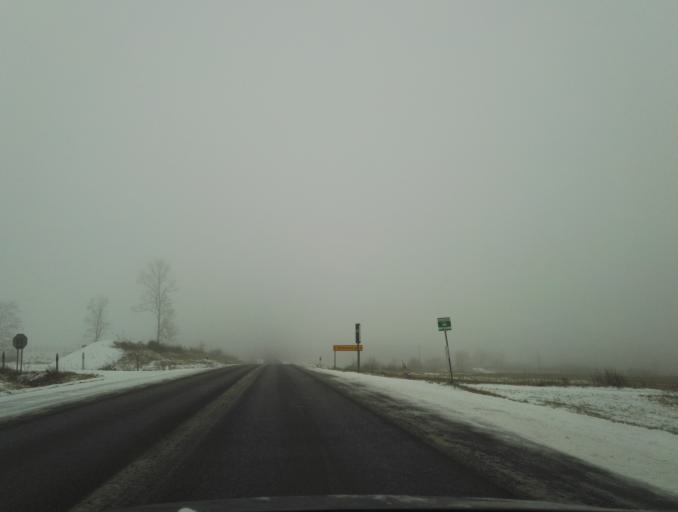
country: SE
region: Kronoberg
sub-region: Vaxjo Kommun
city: Gemla
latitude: 56.8486
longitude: 14.7194
